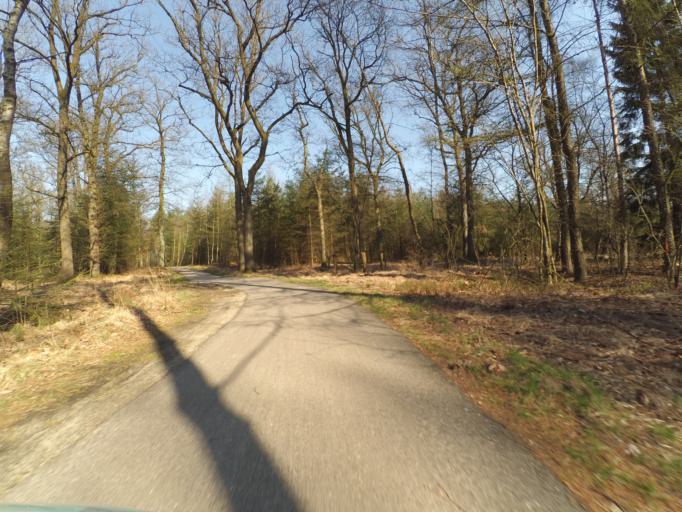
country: NL
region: Gelderland
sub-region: Gemeente Ede
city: Otterlo
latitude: 52.1042
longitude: 5.8533
